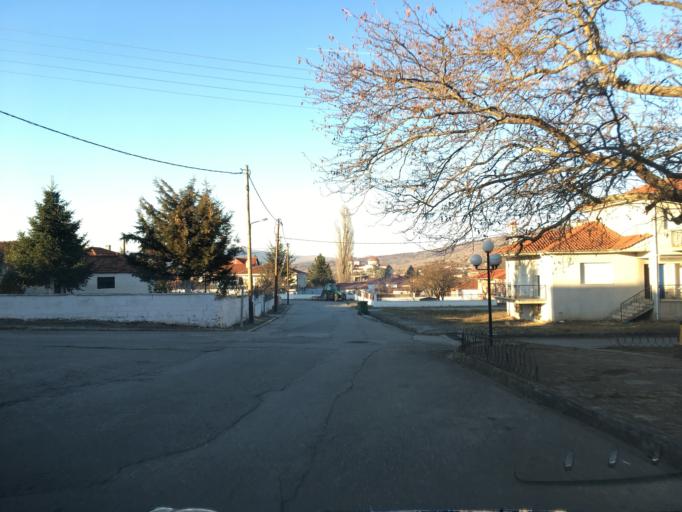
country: GR
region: West Macedonia
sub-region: Nomos Kozanis
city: Kozani
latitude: 40.2862
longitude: 21.7333
